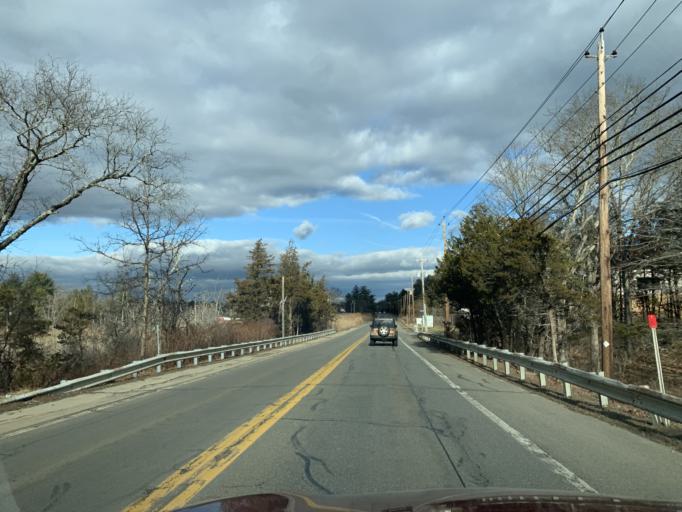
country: US
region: Massachusetts
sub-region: Essex County
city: Newburyport
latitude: 42.7807
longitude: -70.8824
